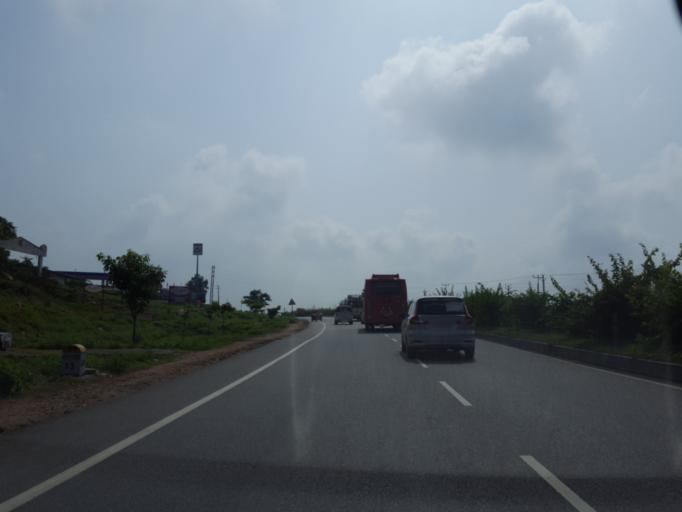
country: IN
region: Telangana
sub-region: Rangareddi
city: Ghatkesar
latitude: 17.2803
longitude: 78.7860
